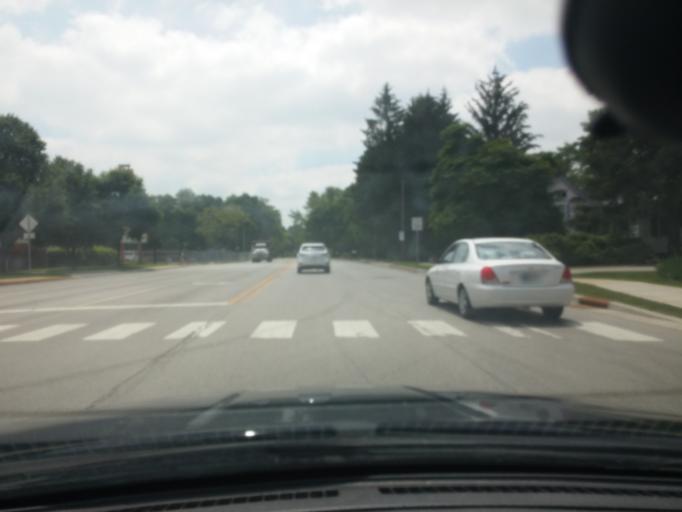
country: US
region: Indiana
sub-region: Tippecanoe County
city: West Lafayette
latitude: 40.4460
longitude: -86.9217
